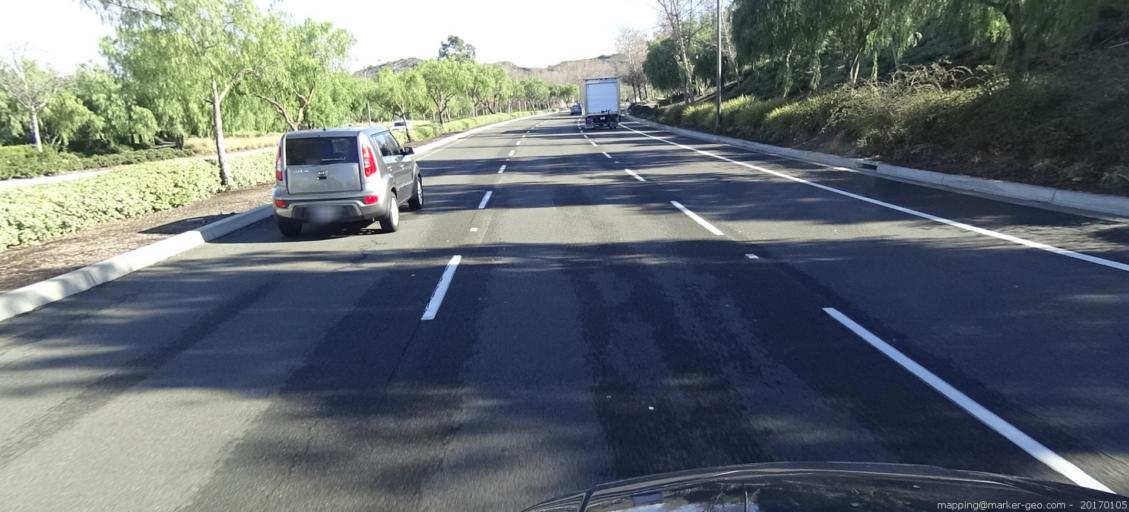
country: US
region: California
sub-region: Orange County
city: Ladera Ranch
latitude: 33.5663
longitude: -117.6407
